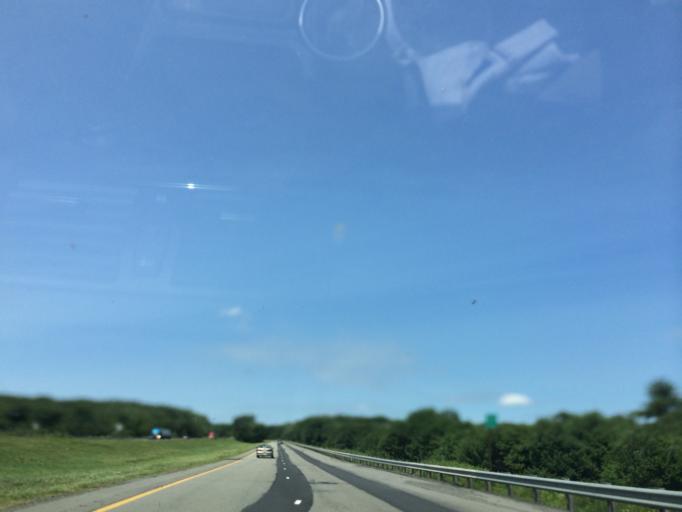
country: US
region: Pennsylvania
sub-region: Pike County
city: Sunrise Lake
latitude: 41.3513
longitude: -74.9646
